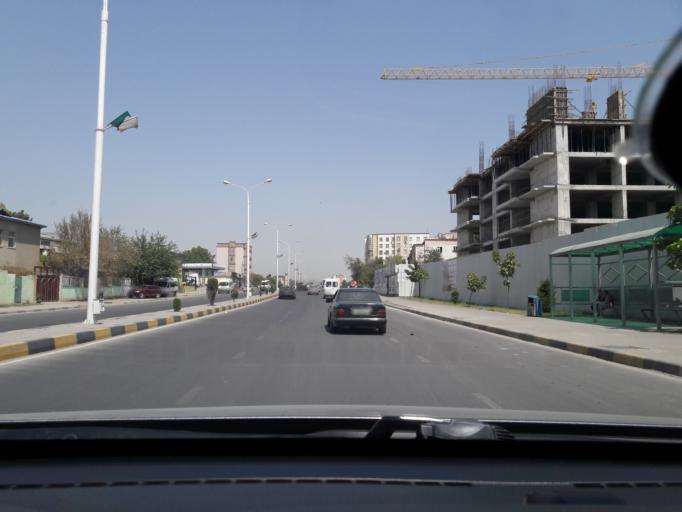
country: TJ
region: Dushanbe
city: Dushanbe
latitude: 38.5893
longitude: 68.7281
